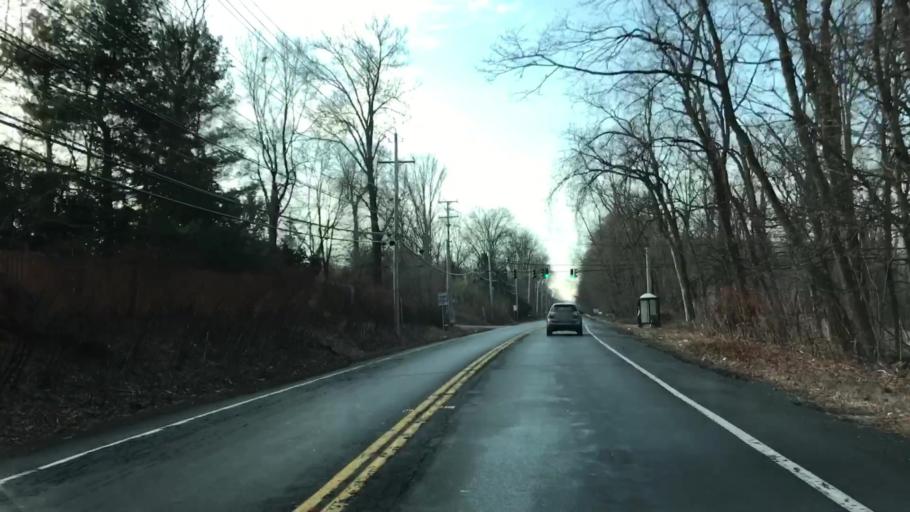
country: US
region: New York
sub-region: Rockland County
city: Congers
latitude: 41.1390
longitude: -73.9372
